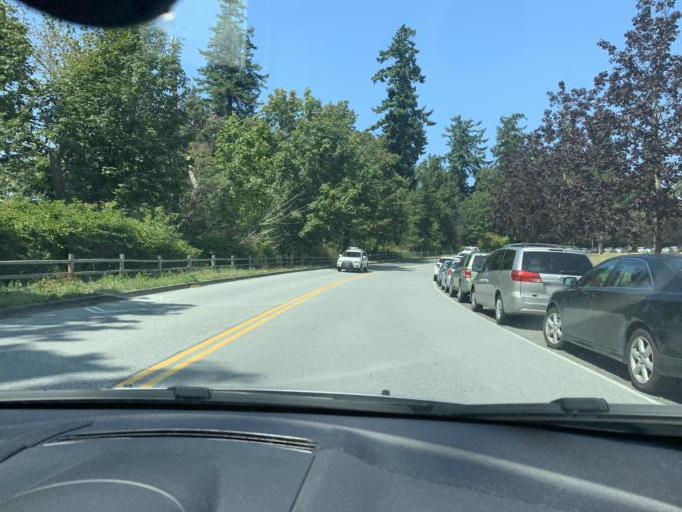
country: CA
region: British Columbia
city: West End
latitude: 49.2568
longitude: -123.2531
